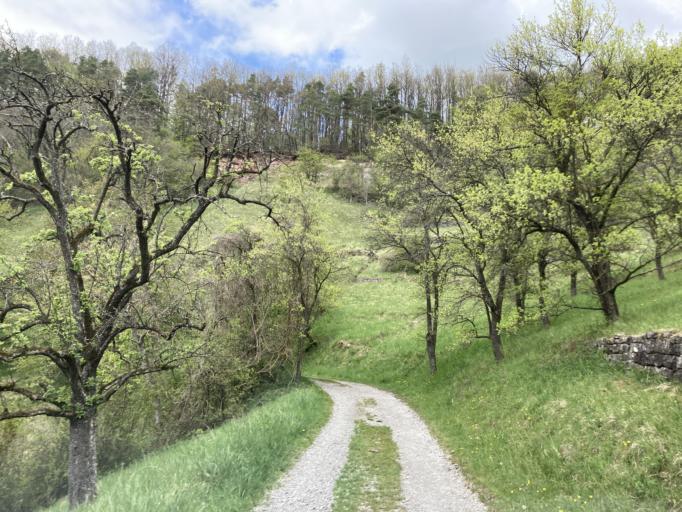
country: DE
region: Baden-Wuerttemberg
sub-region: Tuebingen Region
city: Tuebingen
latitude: 48.5060
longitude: 8.9954
